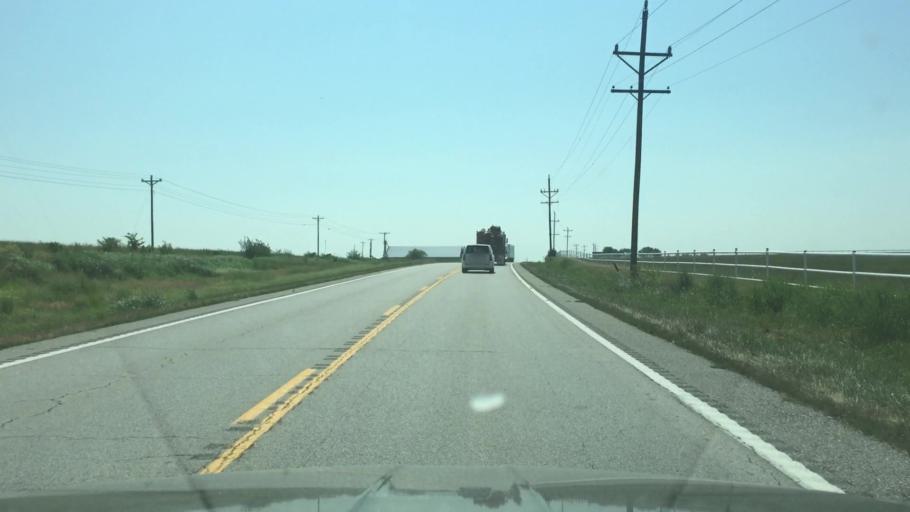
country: US
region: Missouri
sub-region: Moniteau County
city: Tipton
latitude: 38.6698
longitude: -92.8460
